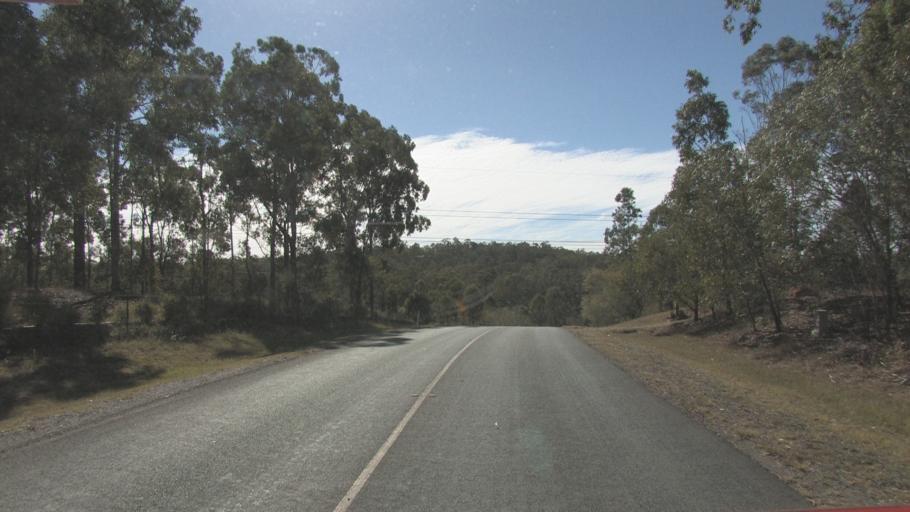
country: AU
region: Queensland
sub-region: Ipswich
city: Springfield Lakes
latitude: -27.7135
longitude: 152.9175
